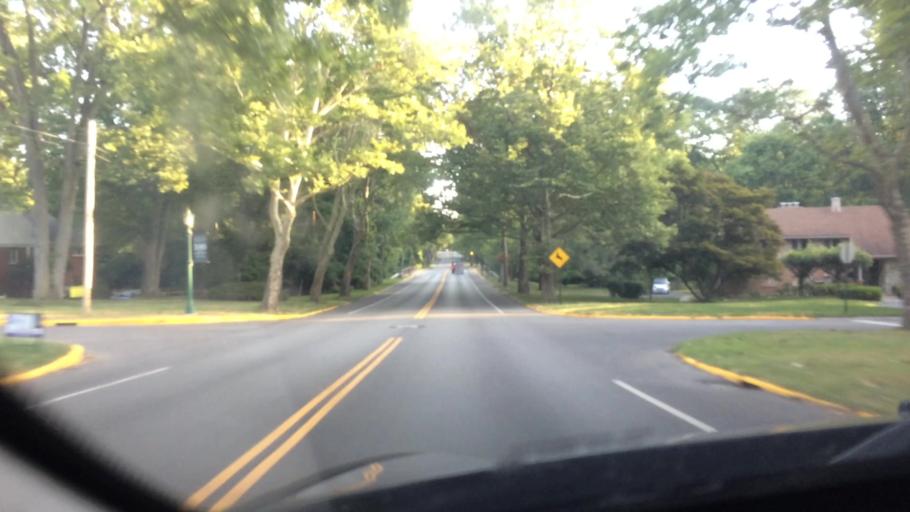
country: US
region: Ohio
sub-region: Lucas County
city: Ottawa Hills
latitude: 41.6641
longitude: -83.6436
